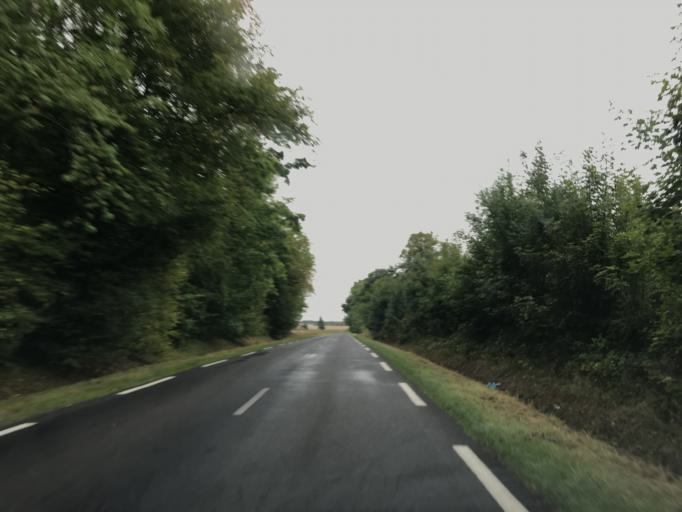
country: FR
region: Haute-Normandie
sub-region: Departement de l'Eure
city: Gravigny
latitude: 49.0190
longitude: 1.2434
